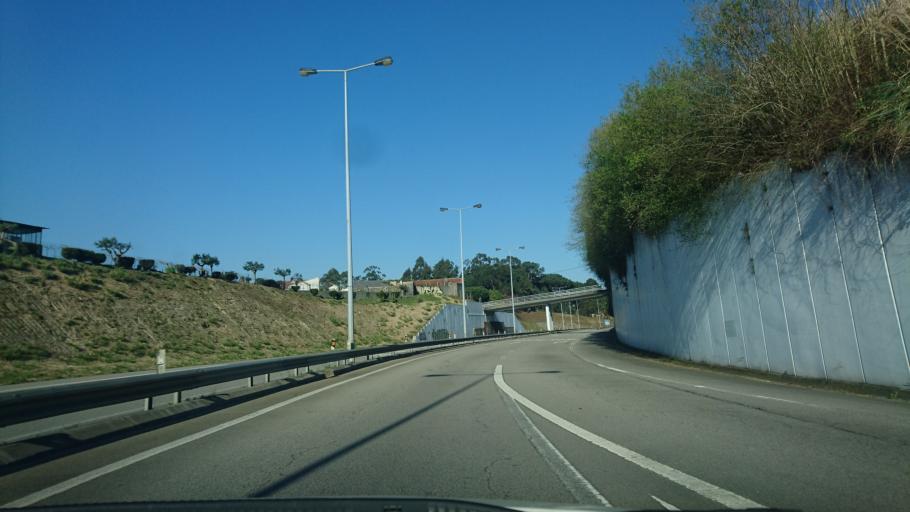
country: PT
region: Porto
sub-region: Vila Nova de Gaia
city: Oliveira do Douro
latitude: 41.1289
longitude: -8.5948
